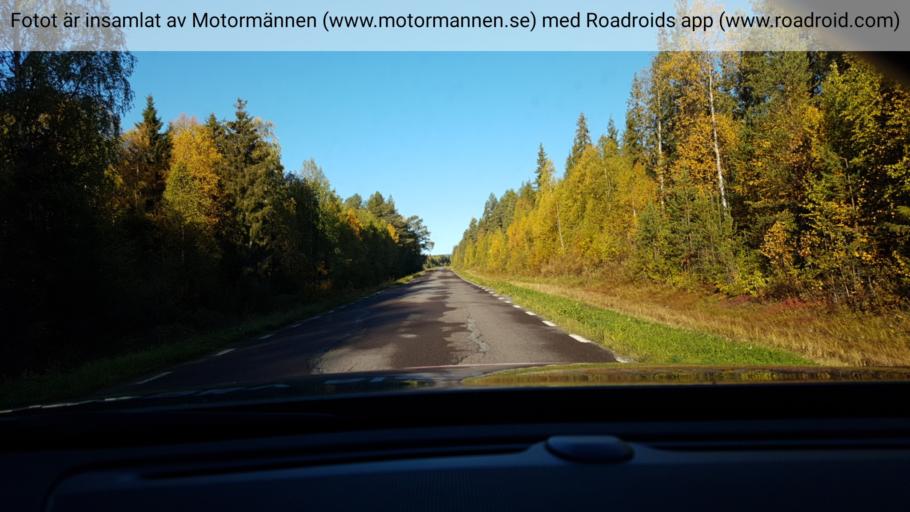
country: SE
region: Norrbotten
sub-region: Bodens Kommun
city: Boden
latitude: 66.0089
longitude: 21.5521
